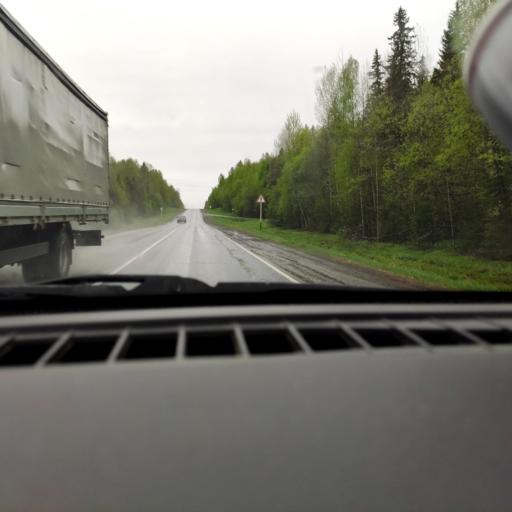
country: RU
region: Perm
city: Perm
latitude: 58.1565
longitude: 56.2504
